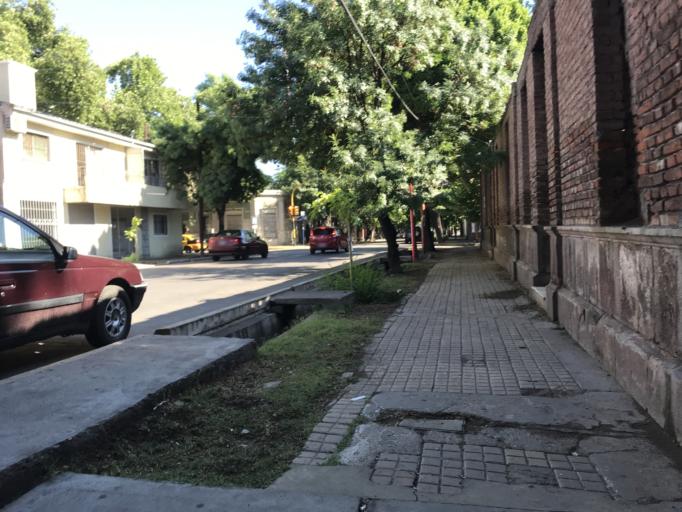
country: AR
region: Mendoza
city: Mendoza
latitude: -32.8842
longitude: -68.8311
